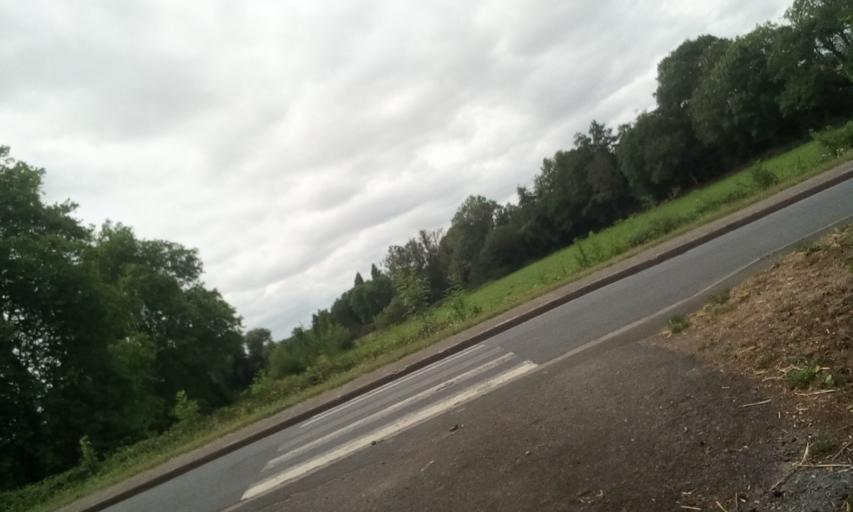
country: FR
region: Lower Normandy
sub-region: Departement du Calvados
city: Fontaine-Etoupefour
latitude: 49.1500
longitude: -0.4562
